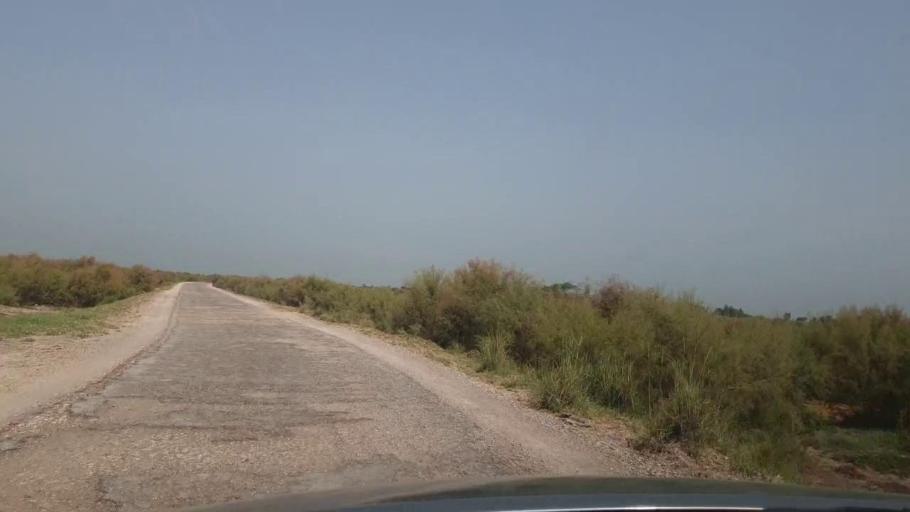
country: PK
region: Sindh
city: Madeji
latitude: 27.8328
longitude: 68.4468
